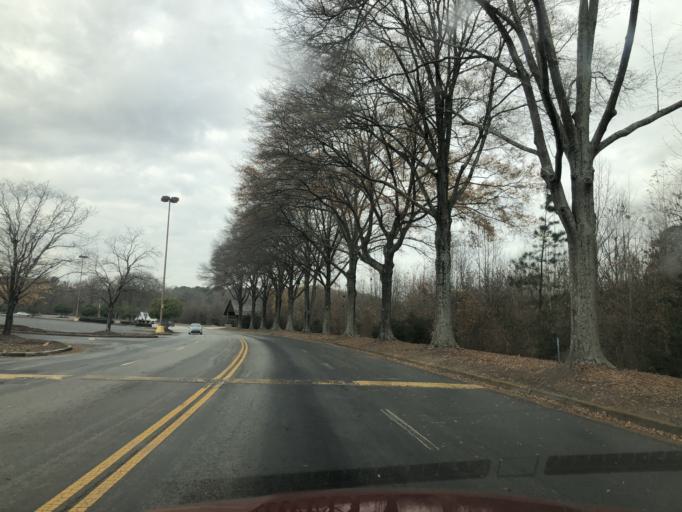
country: US
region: Georgia
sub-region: Clayton County
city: Morrow
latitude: 33.5778
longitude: -84.3510
